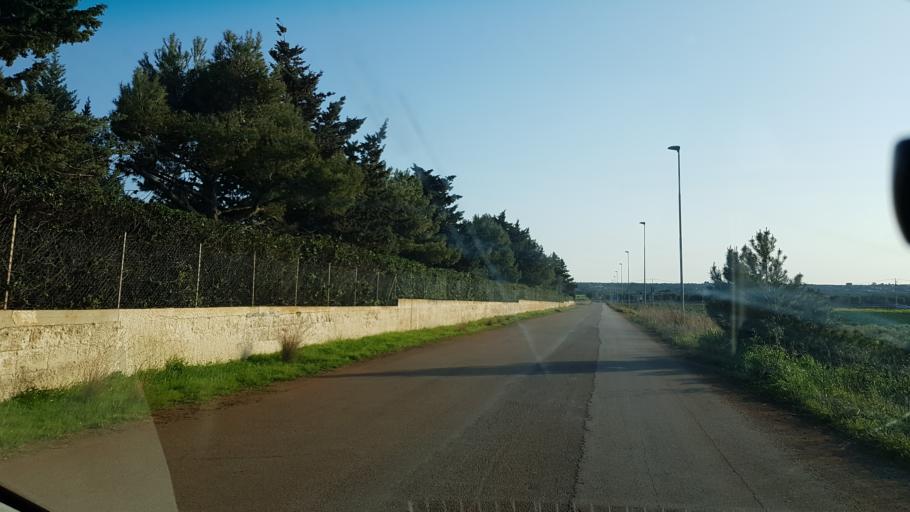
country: IT
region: Apulia
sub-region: Provincia di Brindisi
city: Carovigno
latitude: 40.7390
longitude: 17.7278
